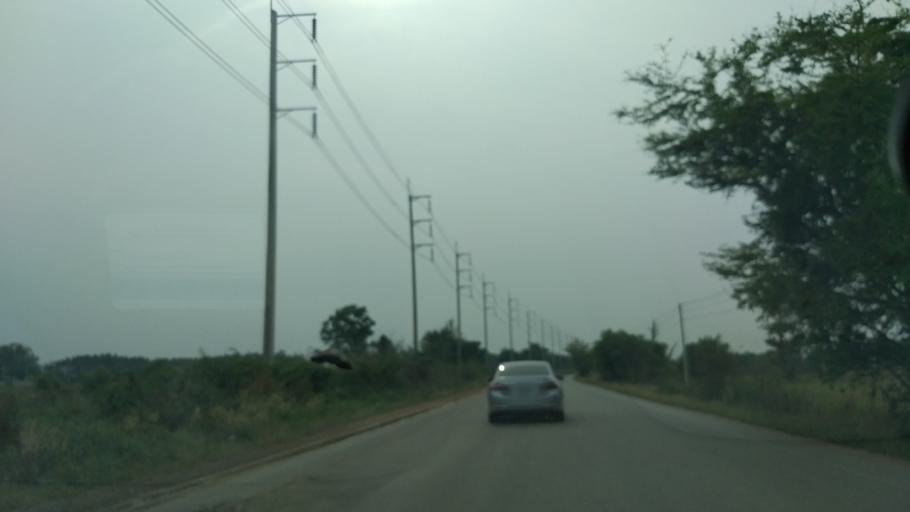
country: TH
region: Chachoengsao
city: Plaeng Yao
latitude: 13.5757
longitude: 101.2494
